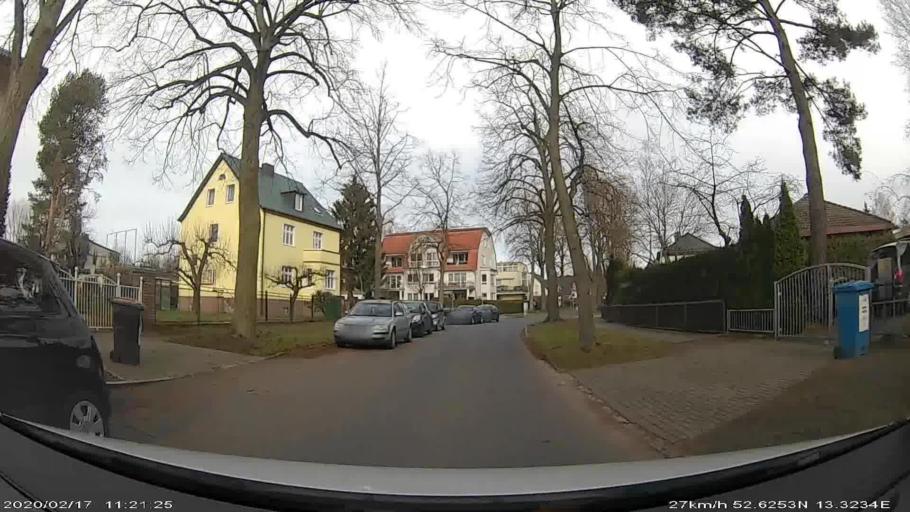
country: DE
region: Brandenburg
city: Glienicke
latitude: 52.6254
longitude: 13.3234
